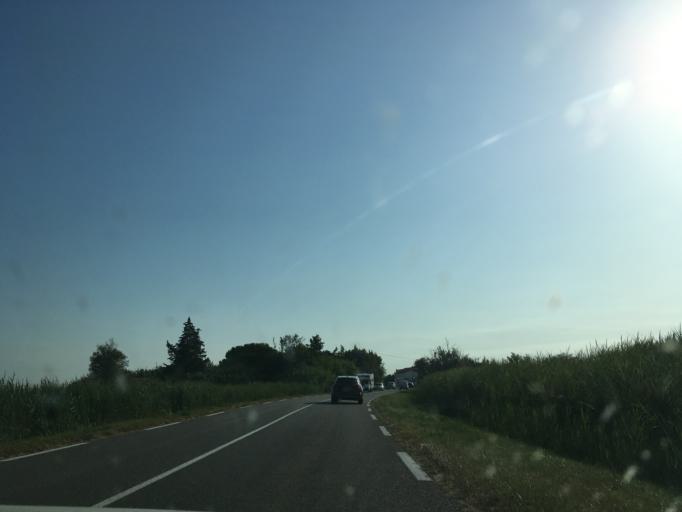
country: FR
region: Languedoc-Roussillon
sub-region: Departement du Gard
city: Fourques
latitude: 43.6430
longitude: 4.5658
